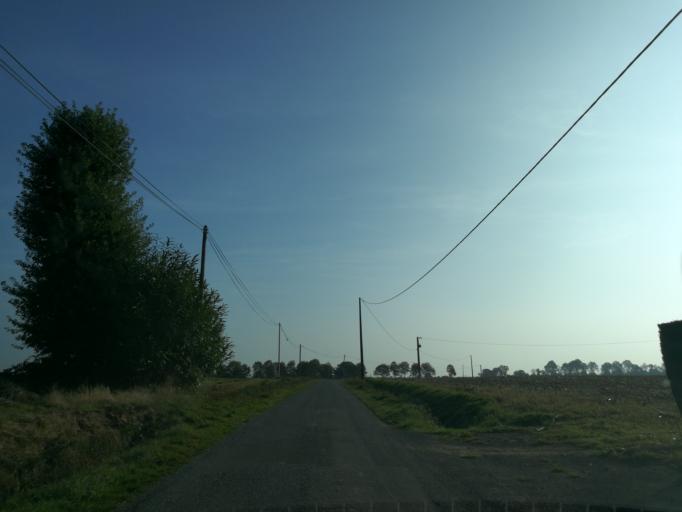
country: FR
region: Brittany
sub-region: Departement d'Ille-et-Vilaine
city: Breteil
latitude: 48.1557
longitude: -1.9056
